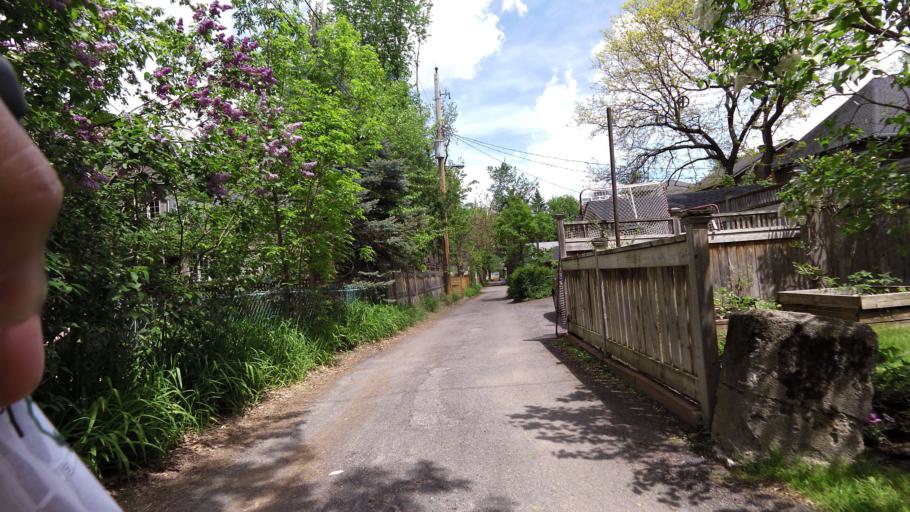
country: CA
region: Ontario
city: Ottawa
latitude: 45.3962
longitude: -75.6900
